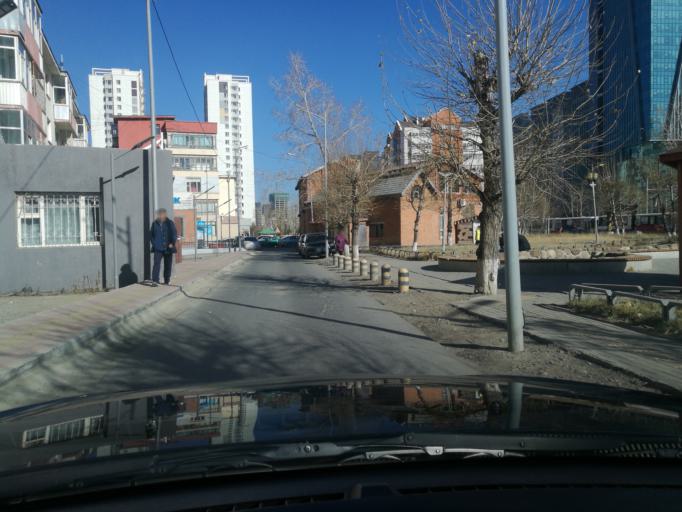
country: MN
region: Ulaanbaatar
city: Ulaanbaatar
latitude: 47.9028
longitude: 106.9097
